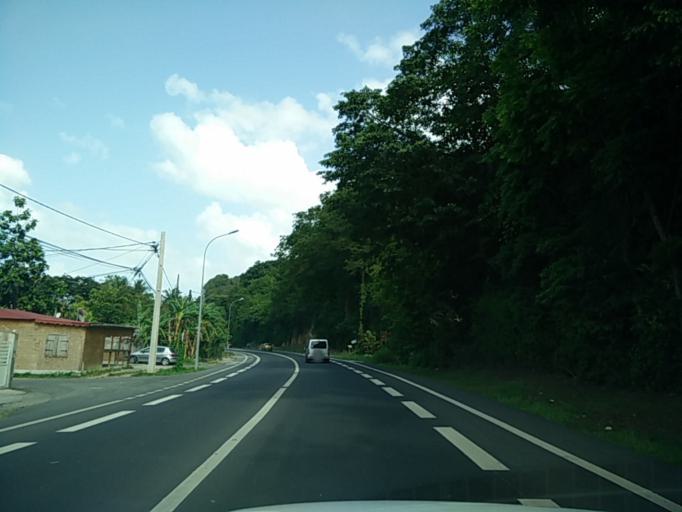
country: GP
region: Guadeloupe
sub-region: Guadeloupe
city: Le Gosier
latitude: 16.2189
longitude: -61.5024
